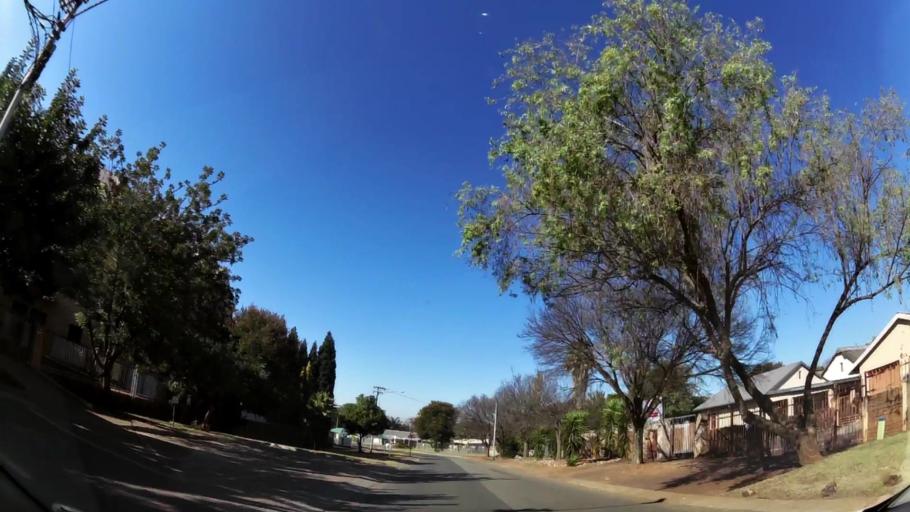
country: ZA
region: Gauteng
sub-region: City of Tshwane Metropolitan Municipality
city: Centurion
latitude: -25.8442
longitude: 28.2080
